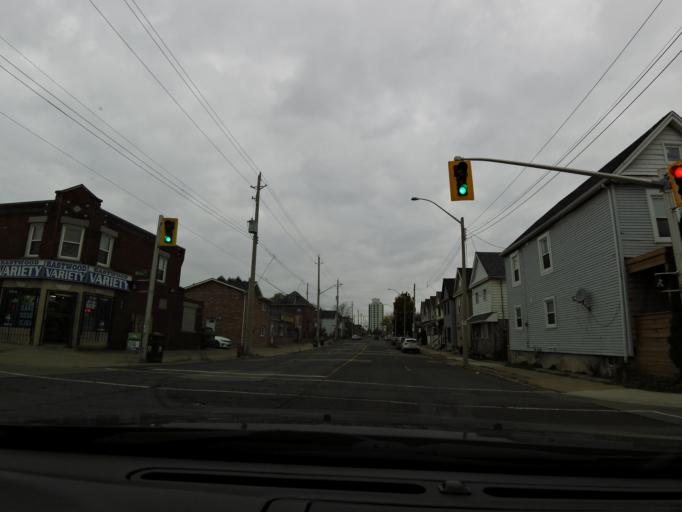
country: CA
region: Ontario
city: Hamilton
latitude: 43.2717
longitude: -79.8569
